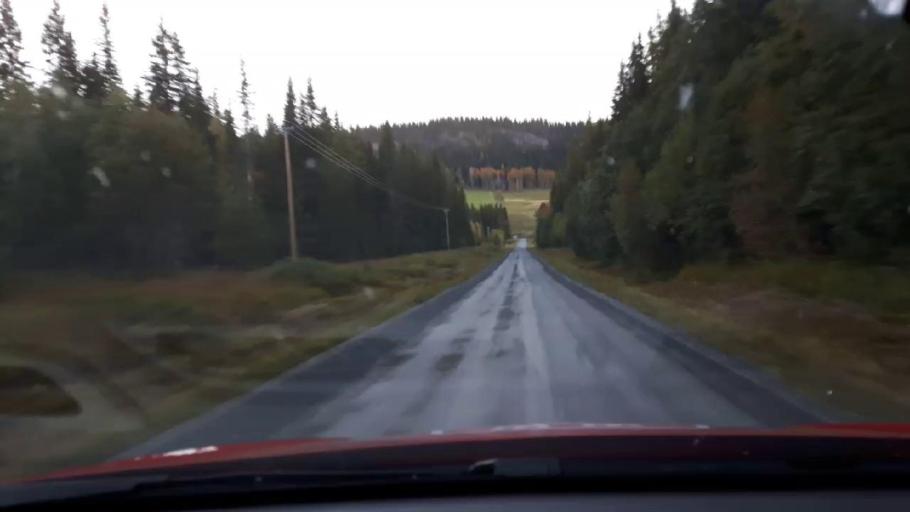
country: SE
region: Jaemtland
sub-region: Krokoms Kommun
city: Krokom
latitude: 63.4842
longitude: 14.2062
